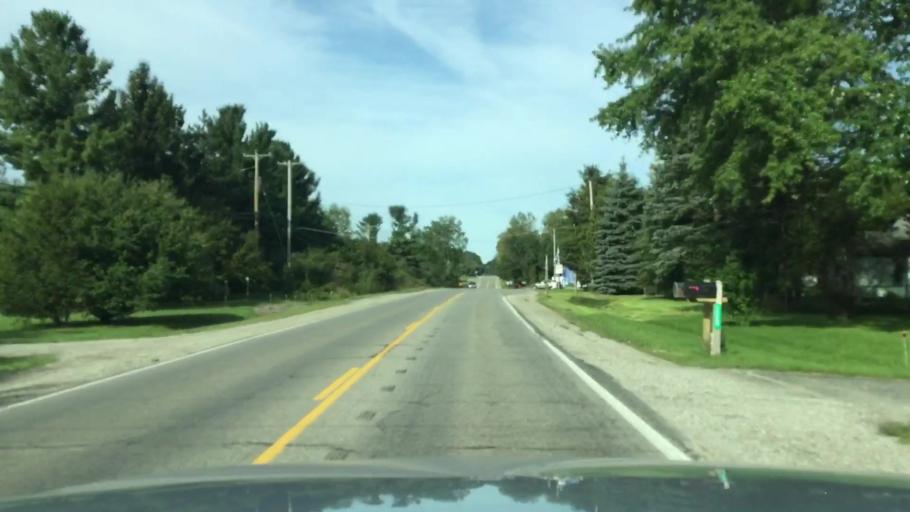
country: US
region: Michigan
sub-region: Genesee County
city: Flushing
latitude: 43.1179
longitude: -83.8234
